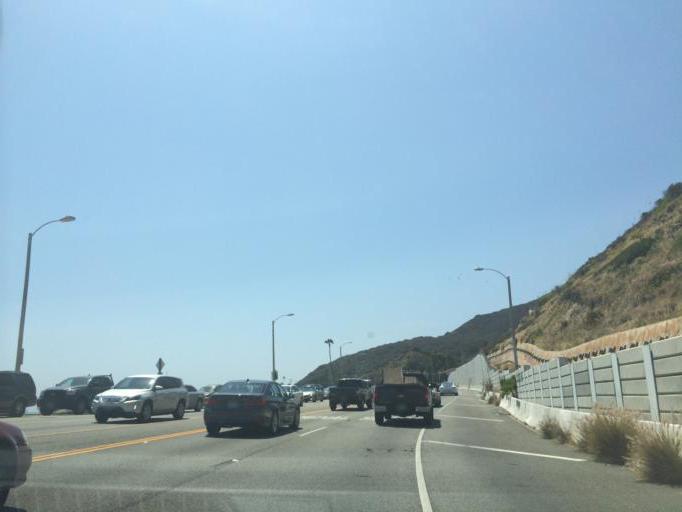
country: US
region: California
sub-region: Los Angeles County
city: Topanga
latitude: 34.0401
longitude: -118.5765
